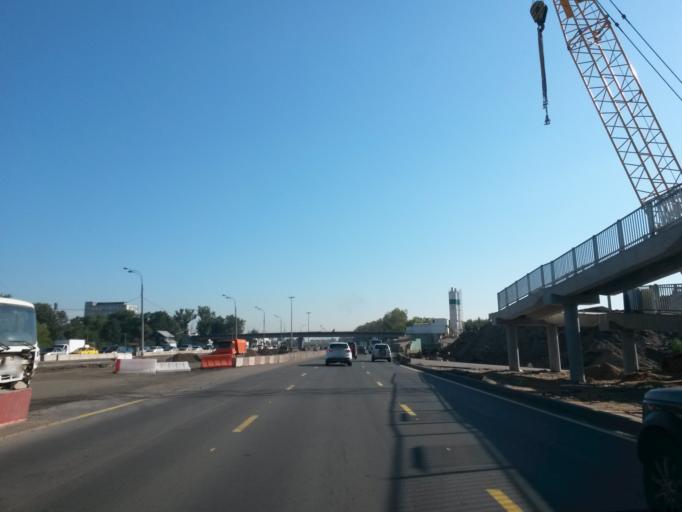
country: RU
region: Moskovskaya
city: Druzhba
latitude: 55.8973
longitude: 37.7518
